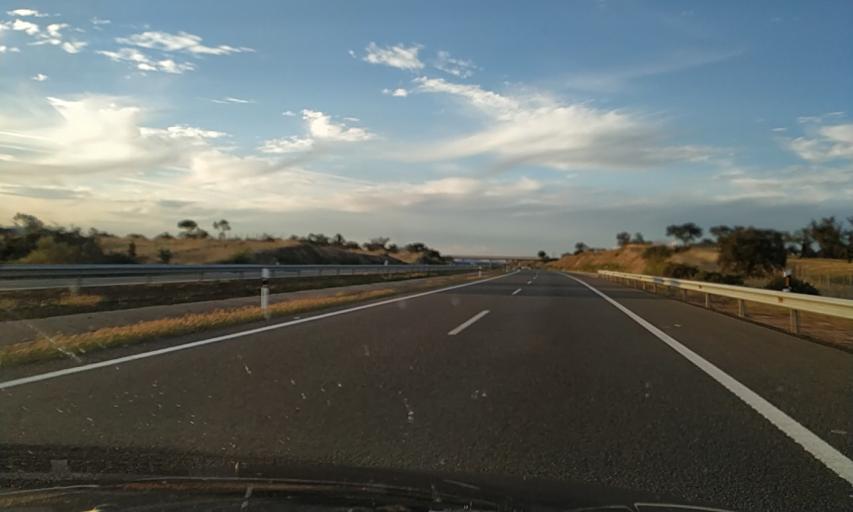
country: ES
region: Extremadura
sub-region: Provincia de Badajoz
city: Aljucen
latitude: 39.0157
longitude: -6.3300
